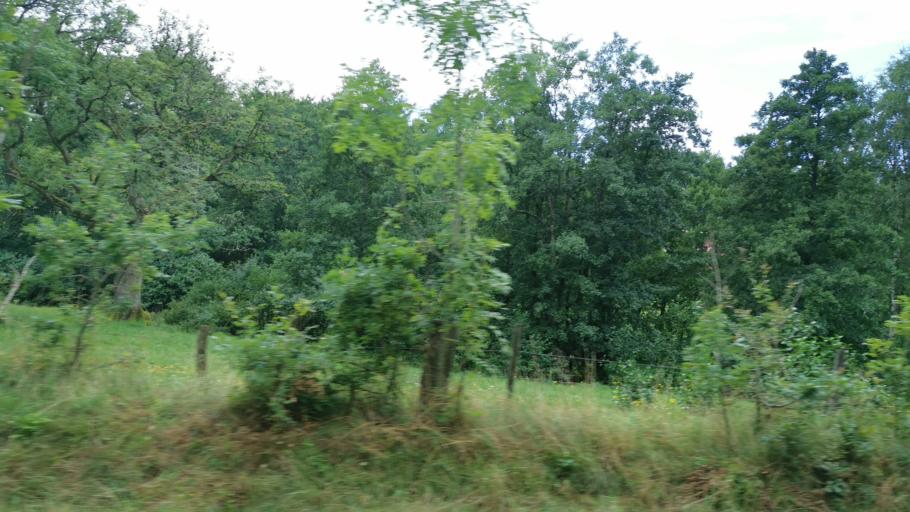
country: SE
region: Vaestra Goetaland
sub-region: Sotenas Kommun
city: Hunnebostrand
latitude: 58.4933
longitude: 11.3401
